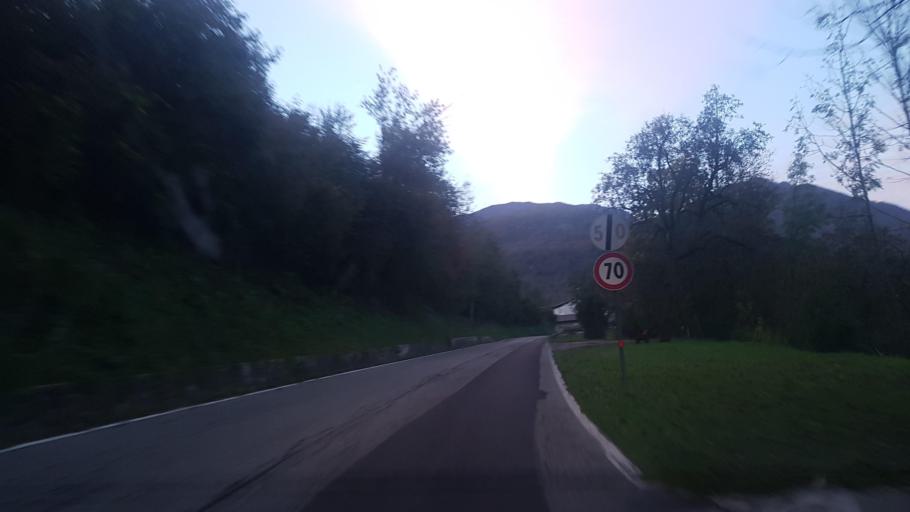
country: IT
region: Friuli Venezia Giulia
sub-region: Provincia di Udine
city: Chiaulis
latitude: 46.3869
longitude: 12.9931
